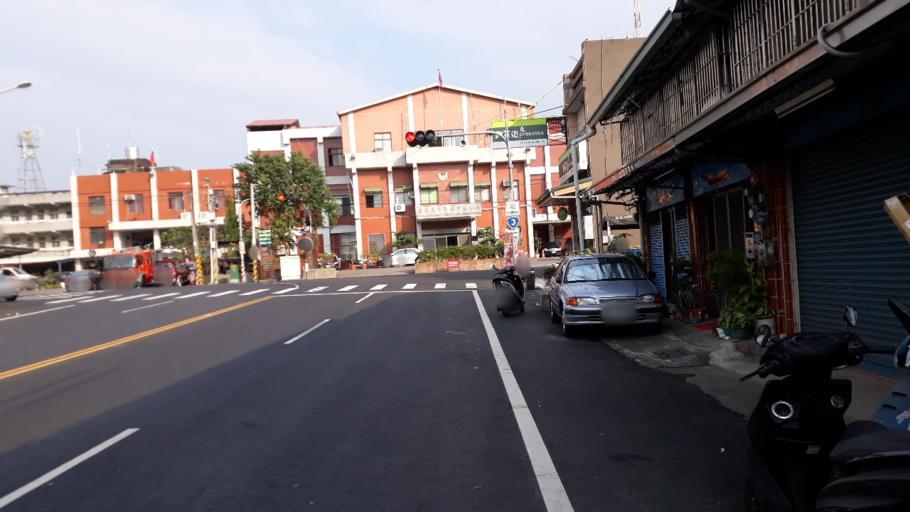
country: TW
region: Taiwan
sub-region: Chiayi
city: Jiayi Shi
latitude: 23.4248
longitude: 120.5231
